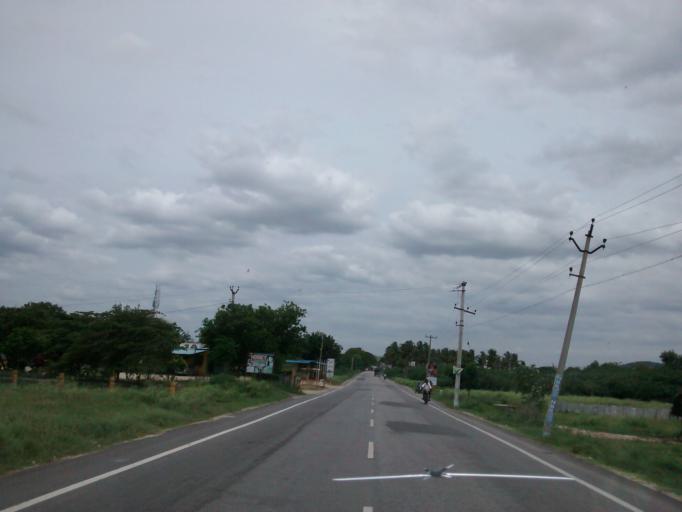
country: IN
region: Andhra Pradesh
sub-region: Chittoor
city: Chittoor
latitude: 13.2817
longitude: 79.0410
